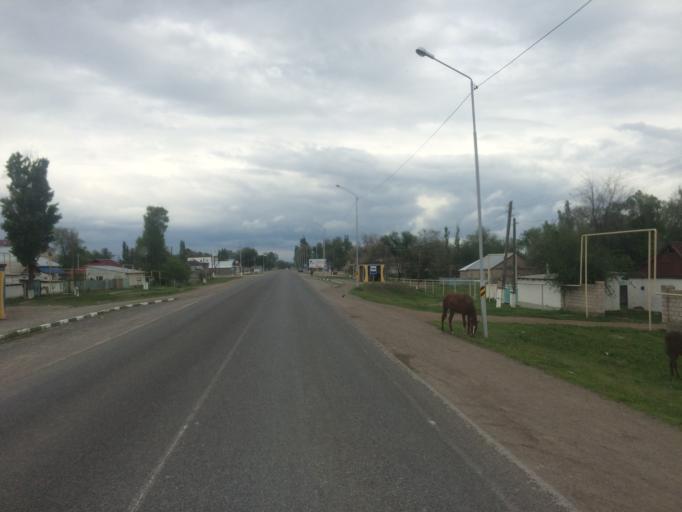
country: KZ
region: Zhambyl
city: Georgiyevka
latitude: 43.2276
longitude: 74.3903
